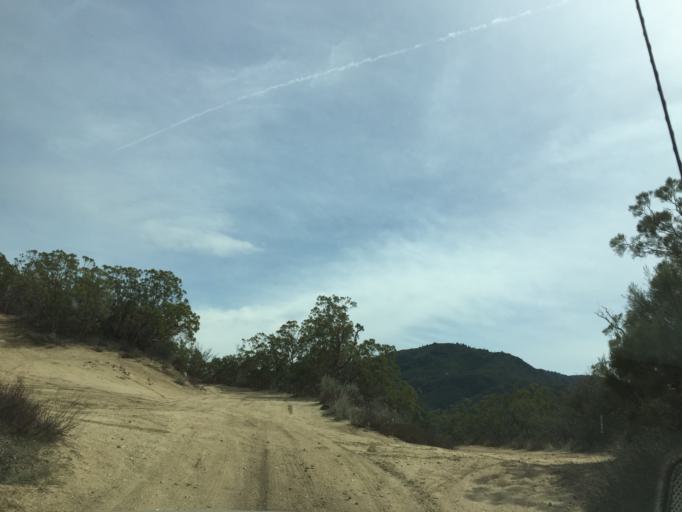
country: US
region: California
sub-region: Riverside County
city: Anza
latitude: 33.6085
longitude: -116.7957
